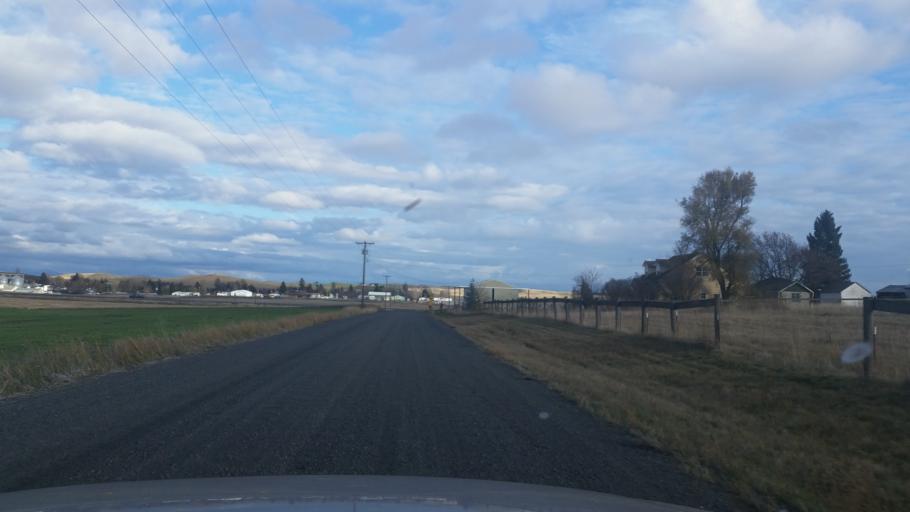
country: US
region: Washington
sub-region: Spokane County
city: Cheney
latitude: 47.4274
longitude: -117.3928
